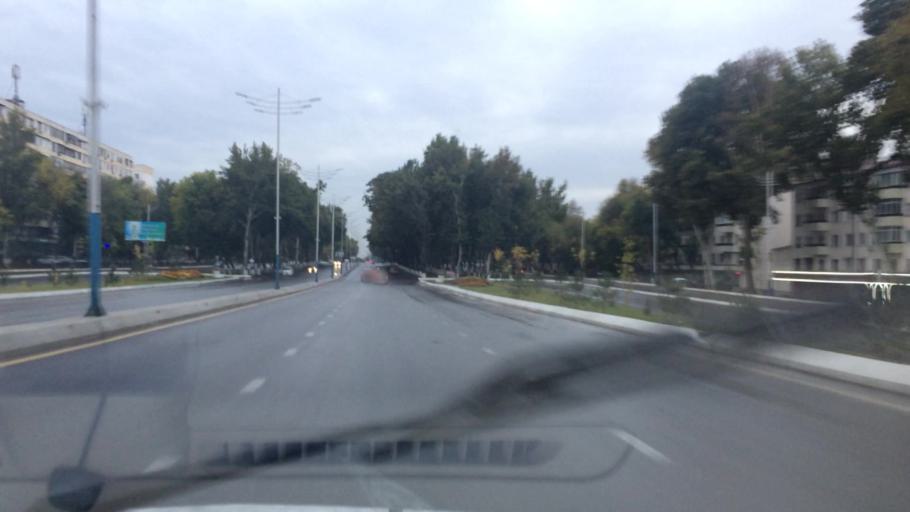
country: UZ
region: Toshkent Shahri
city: Tashkent
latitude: 41.2900
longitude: 69.2210
